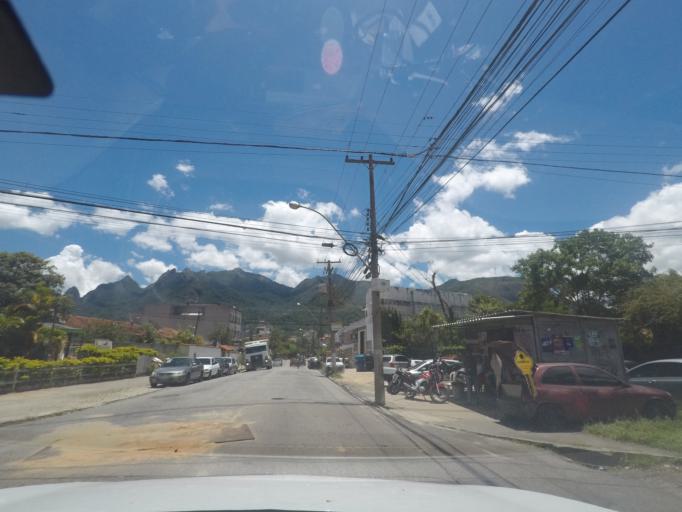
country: BR
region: Rio de Janeiro
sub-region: Teresopolis
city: Teresopolis
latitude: -22.4341
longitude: -42.9711
